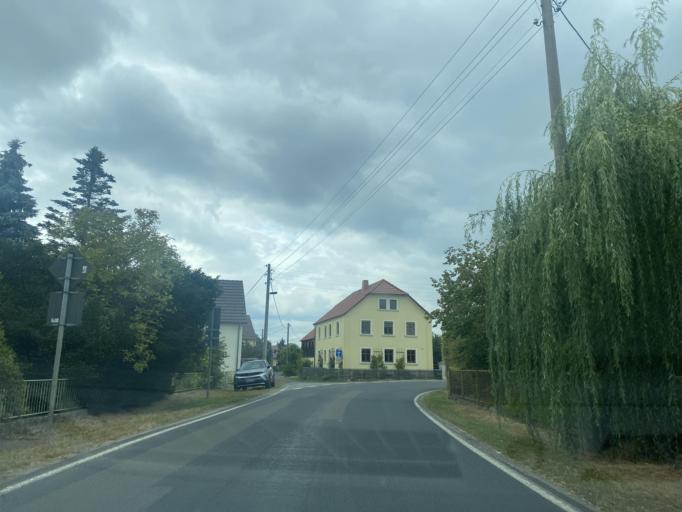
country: DE
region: Saxony
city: Neschwitz
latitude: 51.2894
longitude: 14.3207
